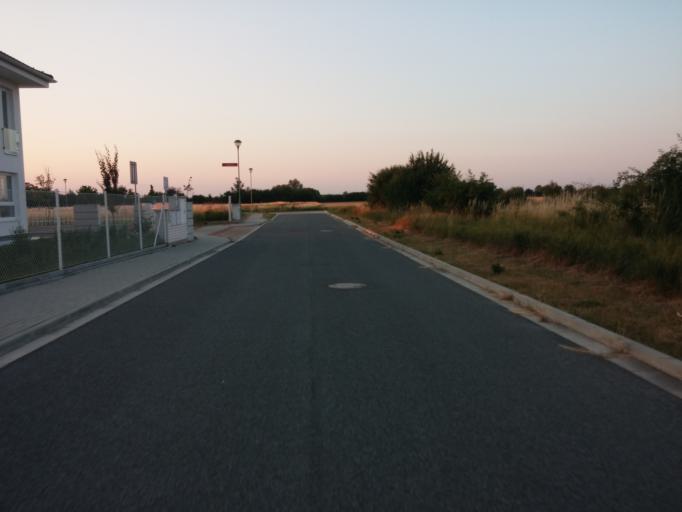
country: CZ
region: Central Bohemia
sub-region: Okres Nymburk
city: Podebrady
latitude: 50.1536
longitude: 15.1252
